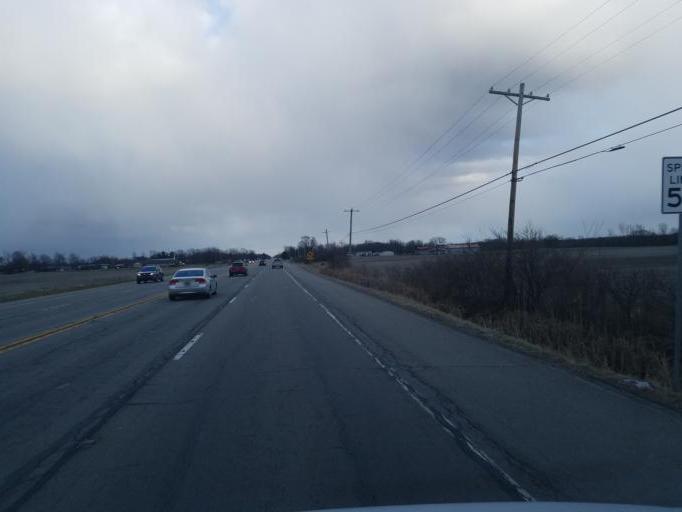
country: US
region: Indiana
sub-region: Hancock County
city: New Palestine
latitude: 39.7800
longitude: -85.8823
